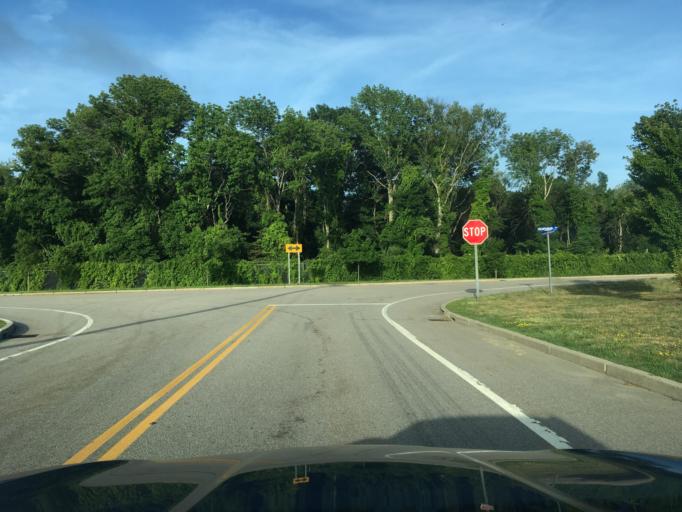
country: US
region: Rhode Island
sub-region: Kent County
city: East Greenwich
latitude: 41.6064
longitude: -71.4286
